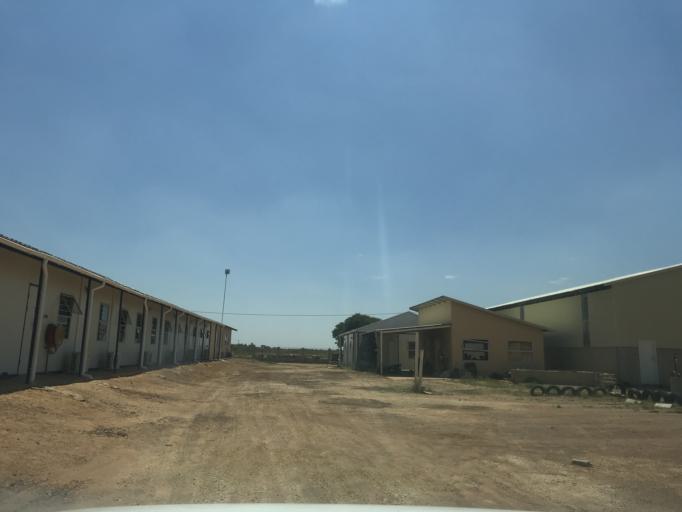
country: BW
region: South East
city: Janeng
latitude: -25.4842
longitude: 25.4250
